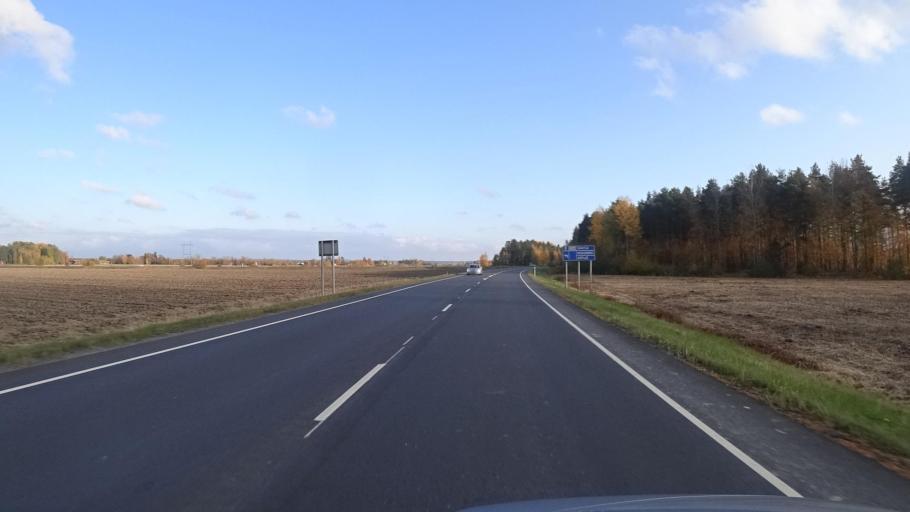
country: FI
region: Satakunta
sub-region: Rauma
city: Saekylae
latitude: 61.0699
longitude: 22.3146
